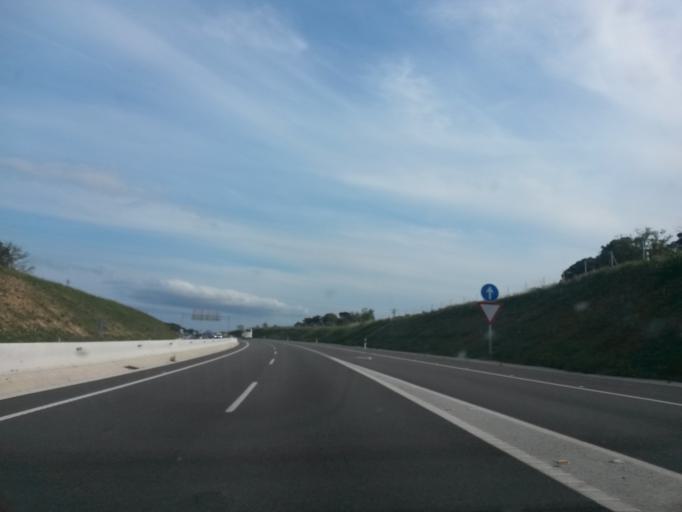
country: ES
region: Catalonia
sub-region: Provincia de Girona
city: Sils
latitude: 41.8324
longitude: 2.7592
